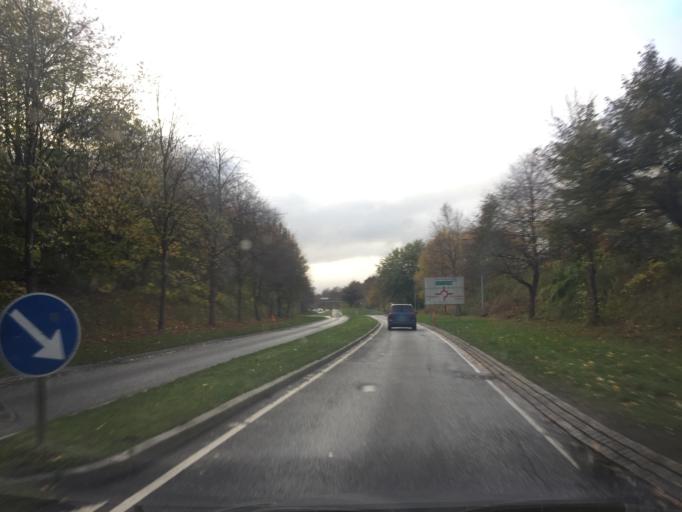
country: DK
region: Capital Region
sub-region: Fredensborg Kommune
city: Humlebaek
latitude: 55.9641
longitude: 12.5283
